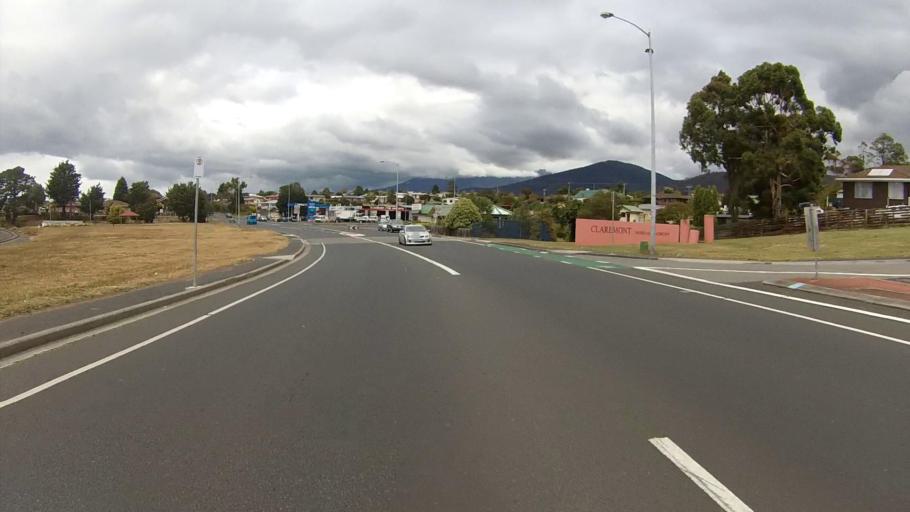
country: AU
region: Tasmania
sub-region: Glenorchy
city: Claremont
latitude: -42.7858
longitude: 147.2518
